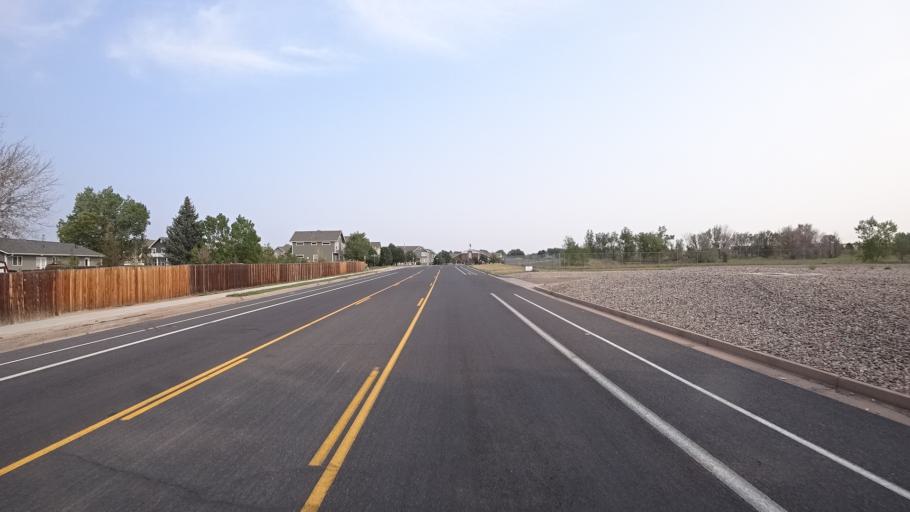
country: US
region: Colorado
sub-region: El Paso County
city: Stratmoor
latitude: 38.8102
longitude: -104.7336
